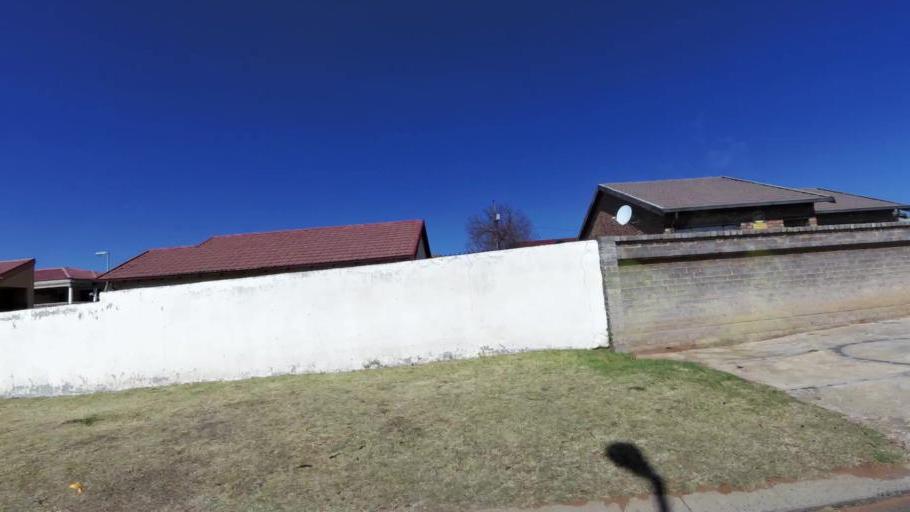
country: ZA
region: Gauteng
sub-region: City of Johannesburg Metropolitan Municipality
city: Johannesburg
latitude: -26.2478
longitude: 27.9827
